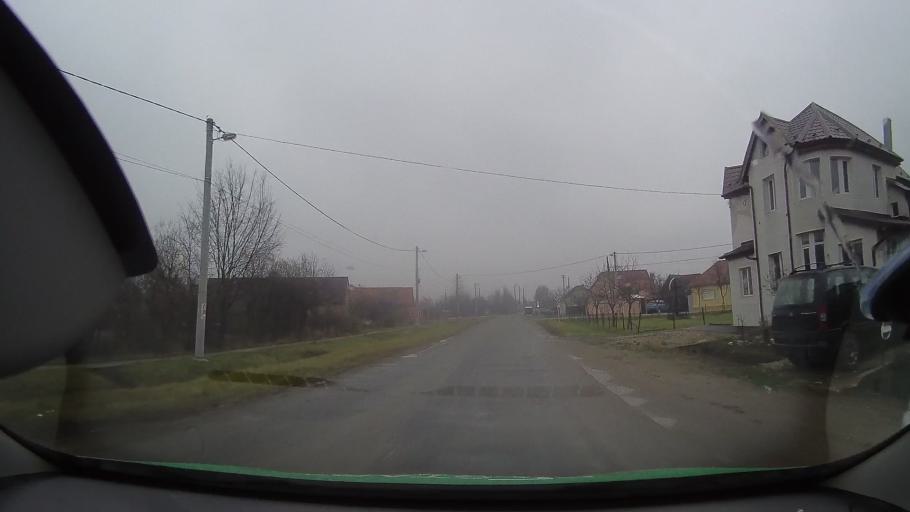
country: RO
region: Bihor
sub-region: Municipiul Salonta
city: Salonta
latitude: 46.8044
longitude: 21.6346
